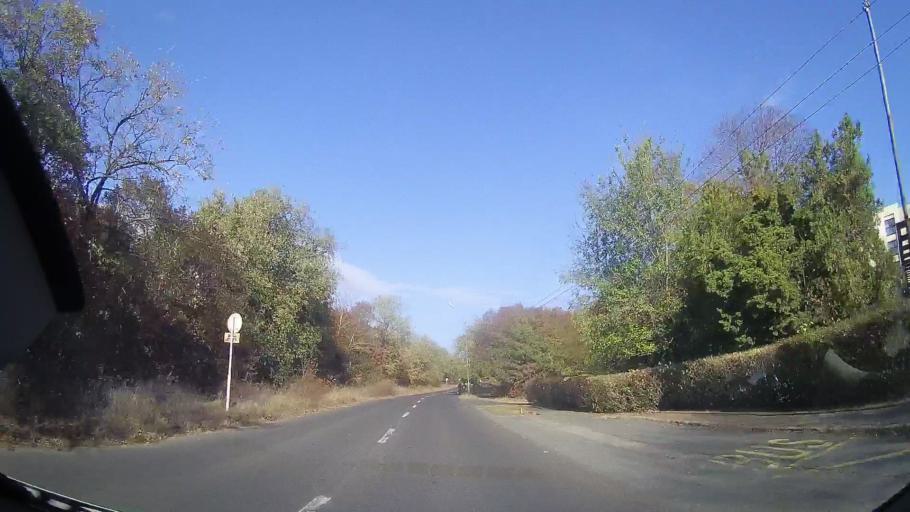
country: RO
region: Constanta
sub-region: Comuna Douazeci si Trei August
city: Douazeci si Trei August
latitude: 43.8730
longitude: 28.5965
